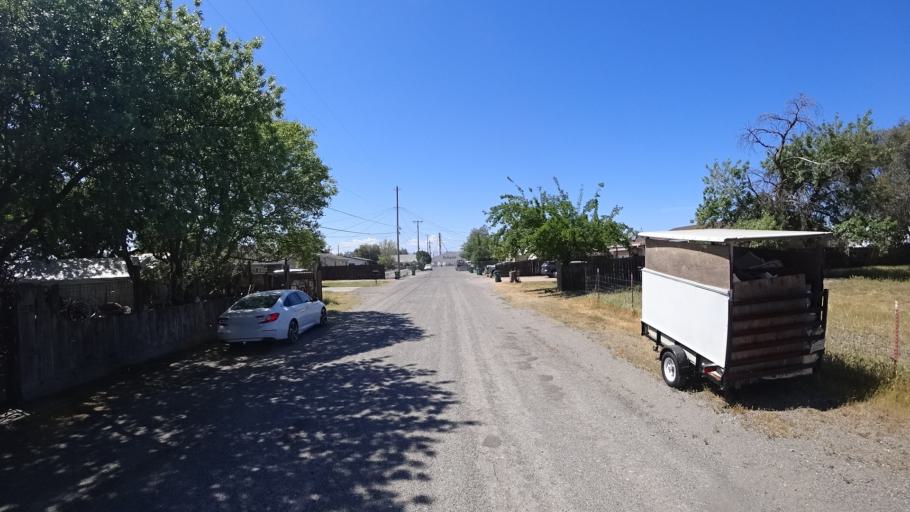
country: US
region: California
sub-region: Glenn County
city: Orland
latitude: 39.7354
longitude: -122.1934
